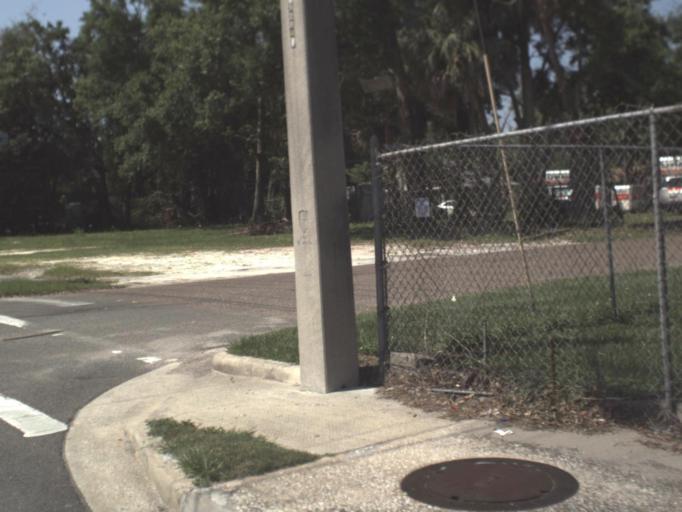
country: US
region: Florida
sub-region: Duval County
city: Jacksonville
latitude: 30.4080
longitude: -81.6875
